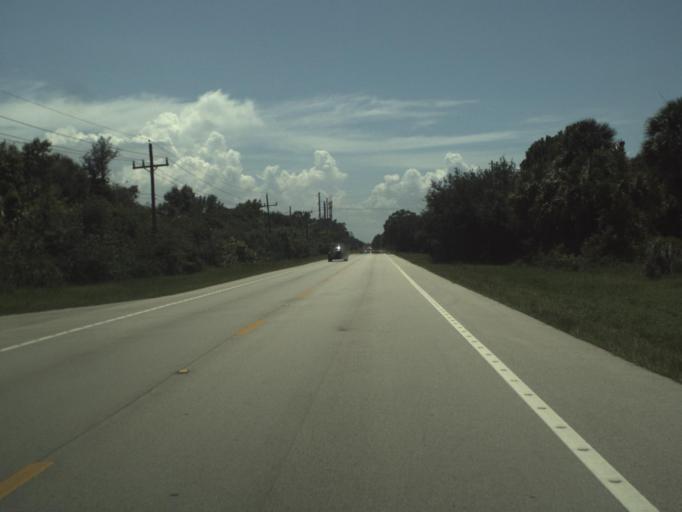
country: US
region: Florida
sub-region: Martin County
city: Indiantown
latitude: 26.9982
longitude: -80.5771
